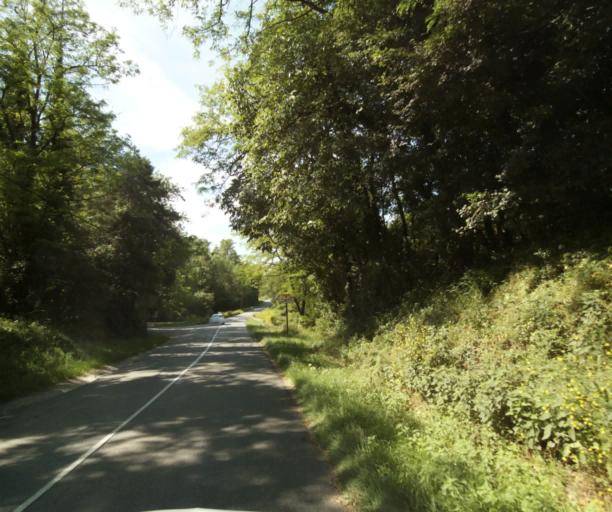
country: FR
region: Rhone-Alpes
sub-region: Departement de la Haute-Savoie
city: Margencel
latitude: 46.3364
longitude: 6.4192
